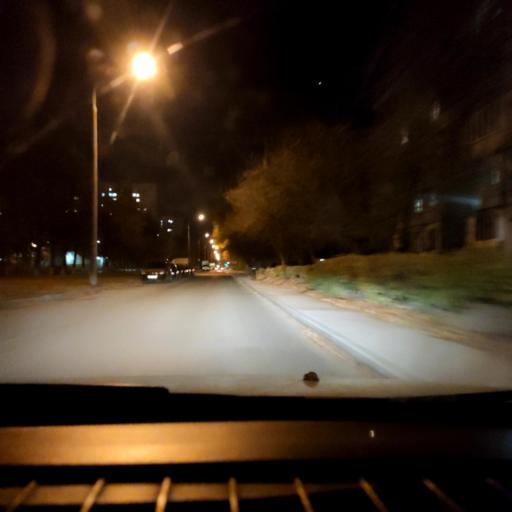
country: RU
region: Samara
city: Tol'yatti
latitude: 53.5255
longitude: 49.3010
